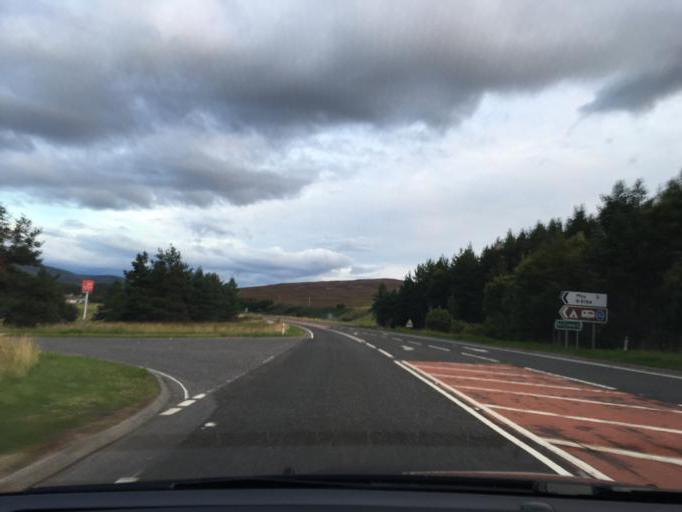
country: GB
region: Scotland
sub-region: Highland
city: Inverness
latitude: 57.3683
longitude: -4.0248
